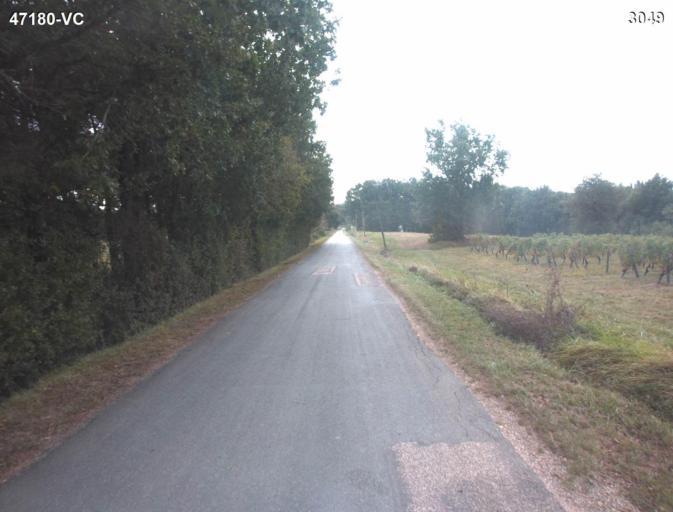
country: FR
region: Aquitaine
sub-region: Departement du Lot-et-Garonne
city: Sainte-Colombe-en-Bruilhois
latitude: 44.1692
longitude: 0.4523
